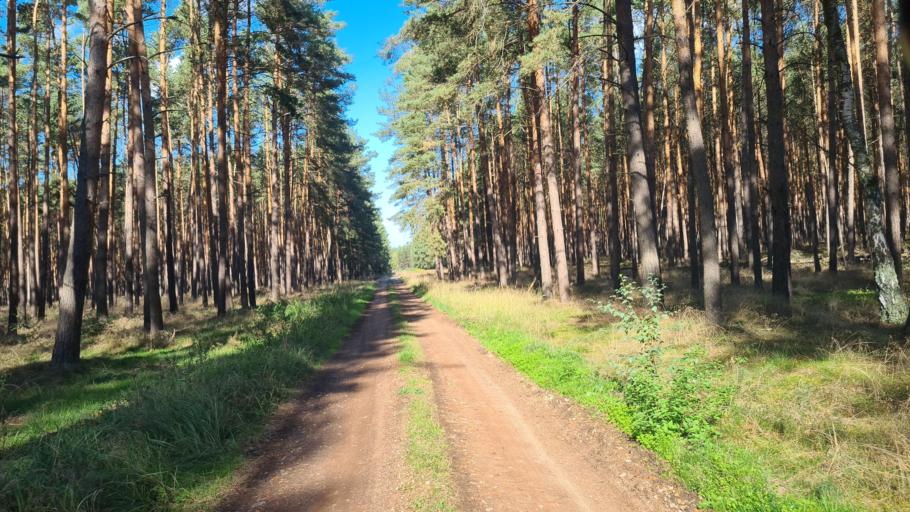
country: DE
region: Brandenburg
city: Hohenbucko
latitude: 51.8254
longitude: 13.5055
